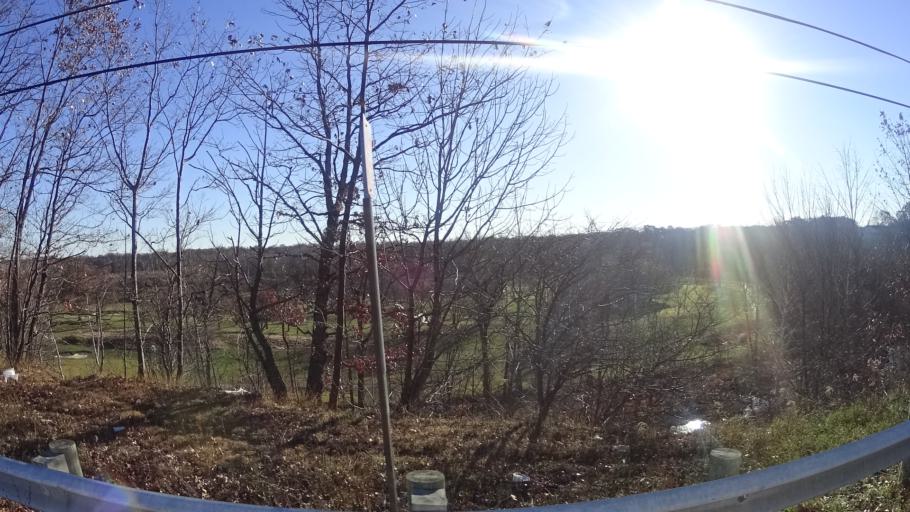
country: US
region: Ohio
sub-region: Lorain County
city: Elyria
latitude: 41.3946
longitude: -82.1055
